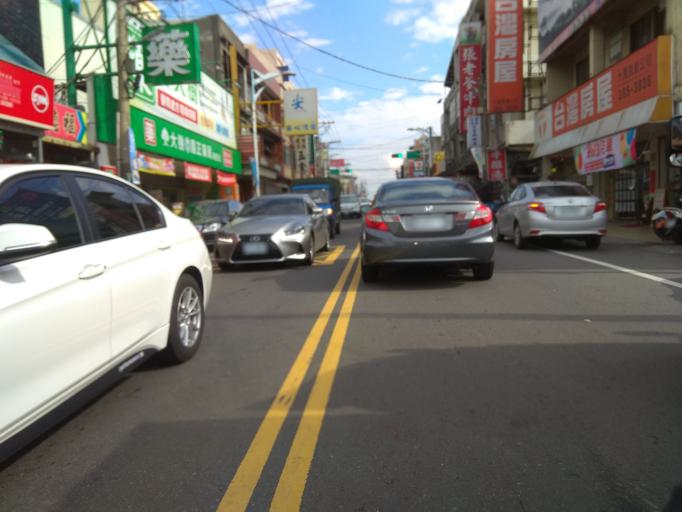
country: TW
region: Taiwan
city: Taoyuan City
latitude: 25.0631
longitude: 121.2000
